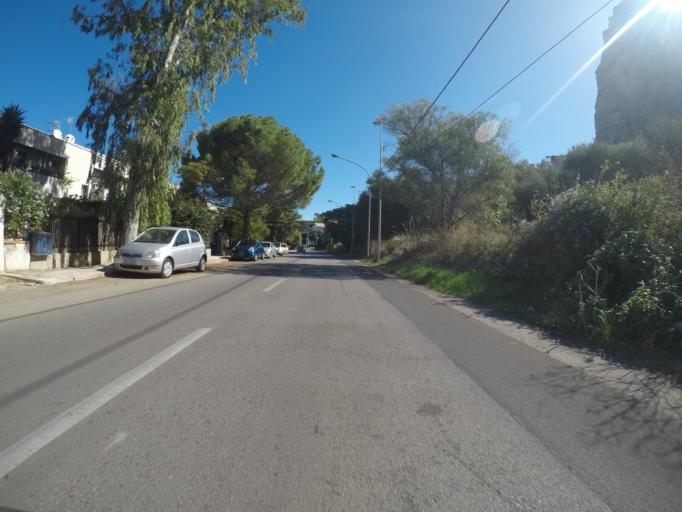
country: IT
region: Sicily
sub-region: Palermo
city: Palermo
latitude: 38.1891
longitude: 13.3535
